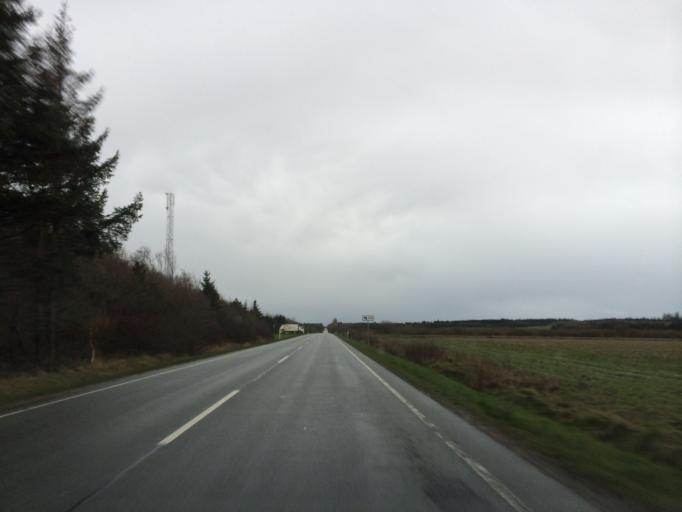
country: DK
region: Central Jutland
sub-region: Ringkobing-Skjern Kommune
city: Tarm
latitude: 55.8647
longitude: 8.5017
